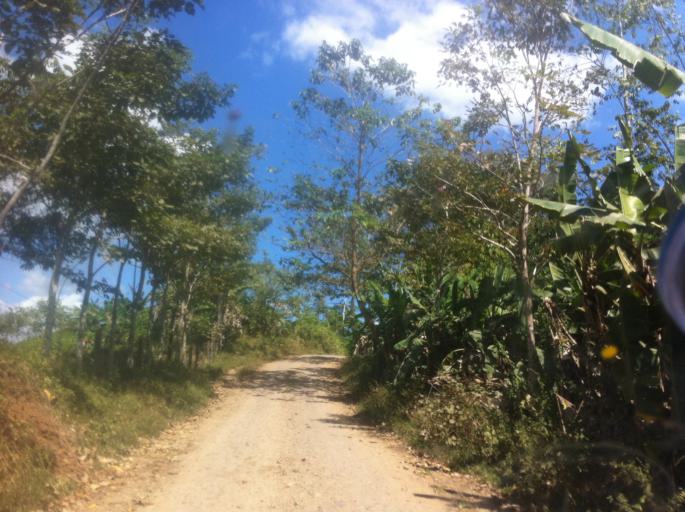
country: CR
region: Alajuela
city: Los Chiles
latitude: 11.2409
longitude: -84.4712
